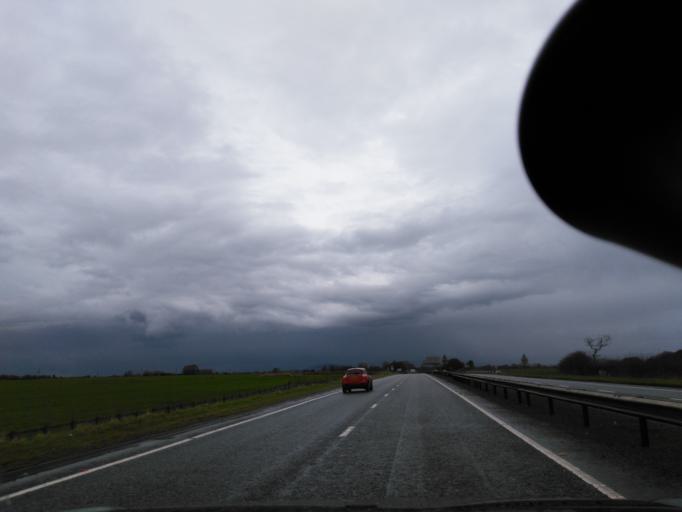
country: GB
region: England
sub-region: North Yorkshire
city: Boroughbridge
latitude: 54.1602
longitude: -1.4057
